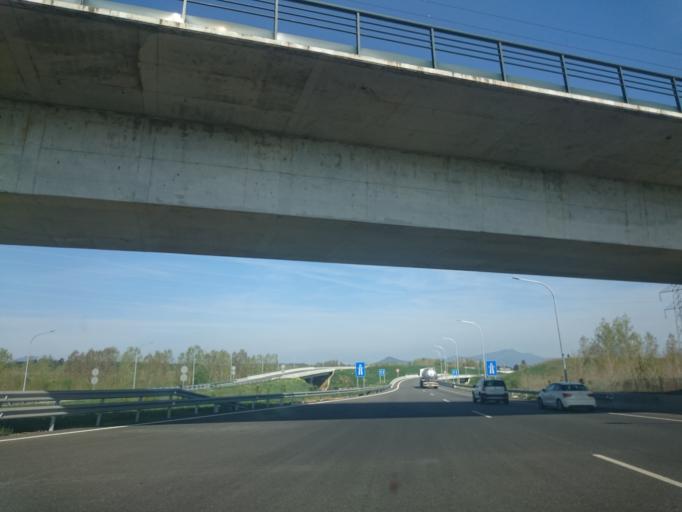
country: ES
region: Catalonia
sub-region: Provincia de Girona
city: Fornells de la Selva
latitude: 41.9297
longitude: 2.7895
